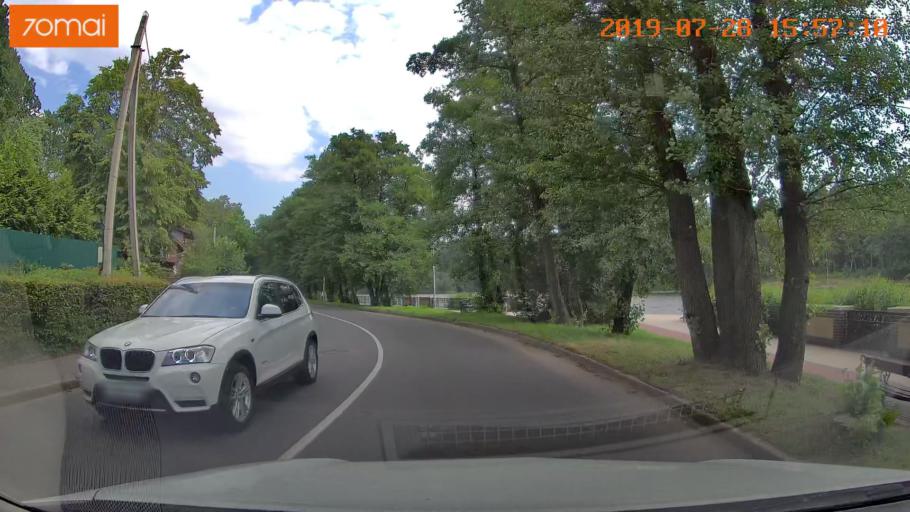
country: RU
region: Kaliningrad
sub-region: Gorod Svetlogorsk
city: Svetlogorsk
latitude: 54.9385
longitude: 20.1527
